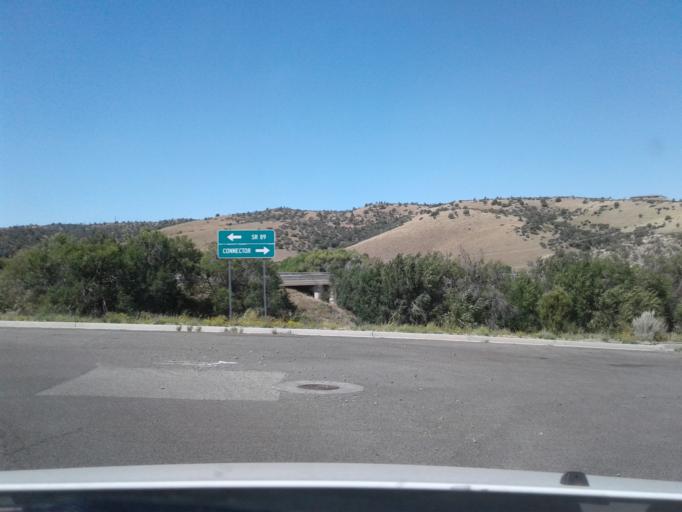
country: US
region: Arizona
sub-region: Yavapai County
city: Prescott
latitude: 34.5561
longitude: -112.4472
